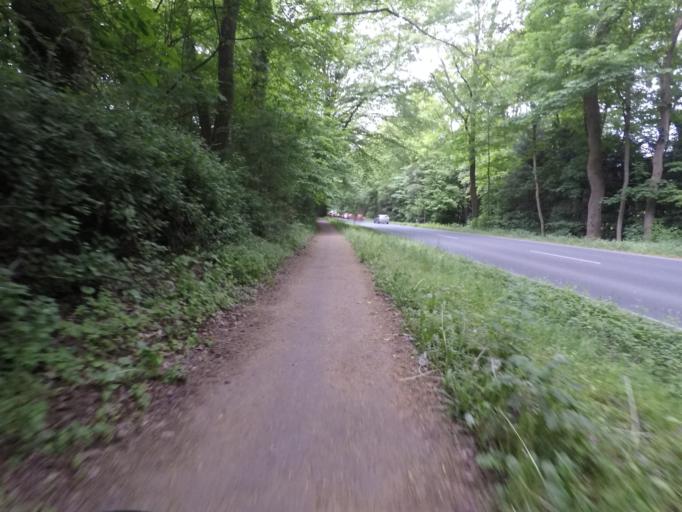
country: DE
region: North Rhine-Westphalia
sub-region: Regierungsbezirk Detmold
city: Bad Salzuflen
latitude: 52.0982
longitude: 8.7550
